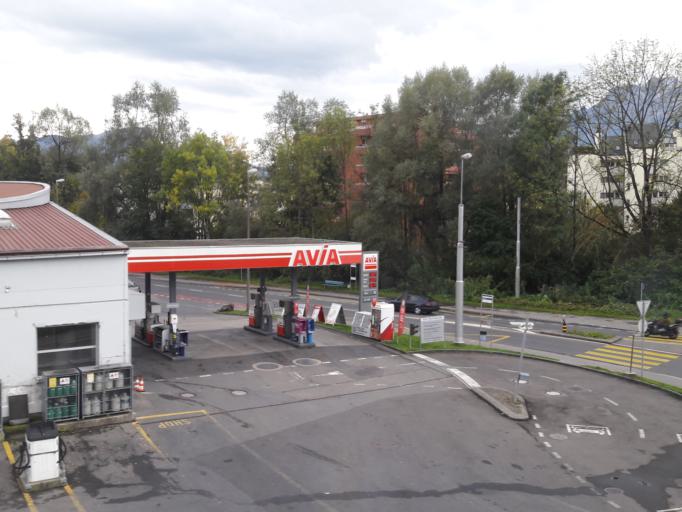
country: CH
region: Lucerne
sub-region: Lucerne-Land District
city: Adligenswil
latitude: 47.0535
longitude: 8.3392
